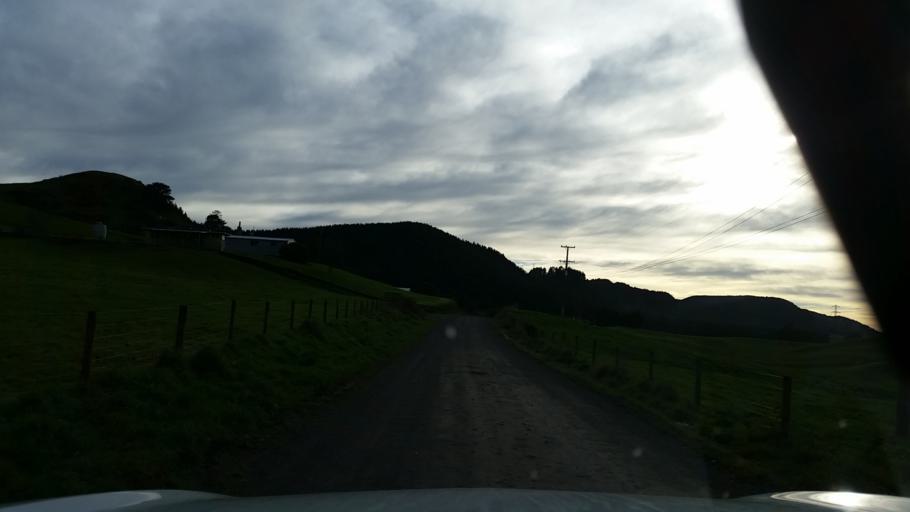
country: NZ
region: Bay of Plenty
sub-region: Rotorua District
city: Rotorua
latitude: -38.2313
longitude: 176.1587
